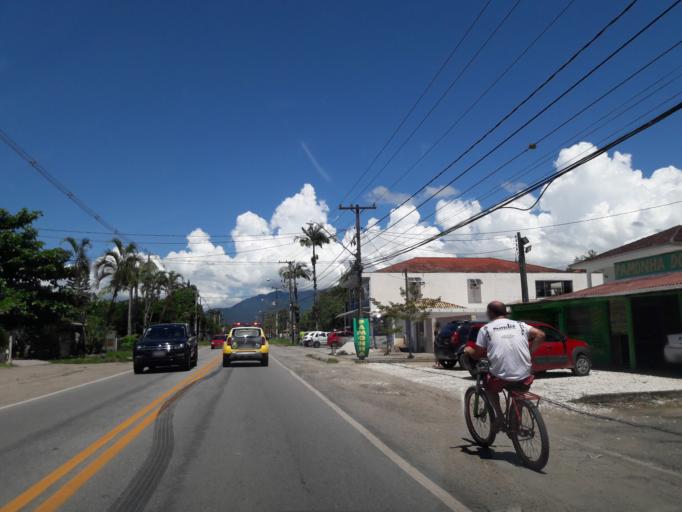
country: BR
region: Parana
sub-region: Antonina
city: Antonina
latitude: -25.4904
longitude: -48.8238
